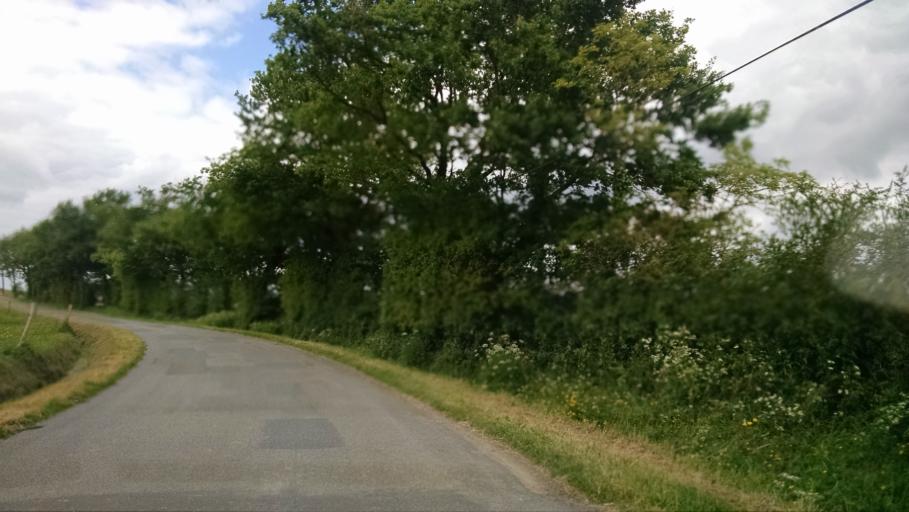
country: FR
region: Pays de la Loire
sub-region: Departement de la Loire-Atlantique
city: Remouille
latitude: 47.0480
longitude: -1.3846
